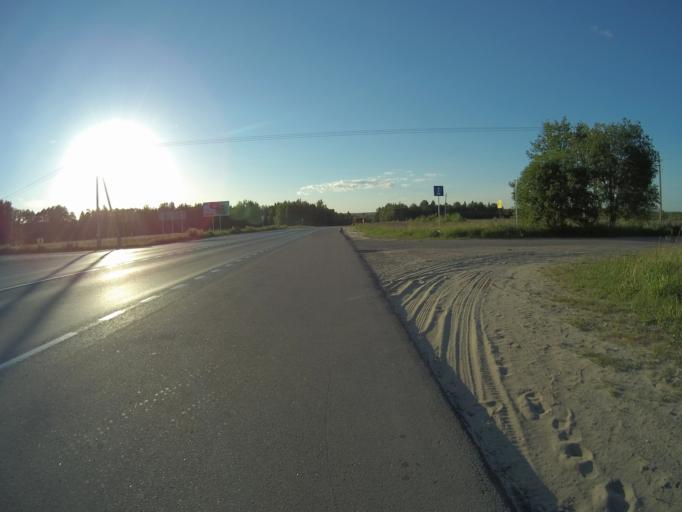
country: RU
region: Vladimir
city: Golovino
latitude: 55.9670
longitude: 40.5516
